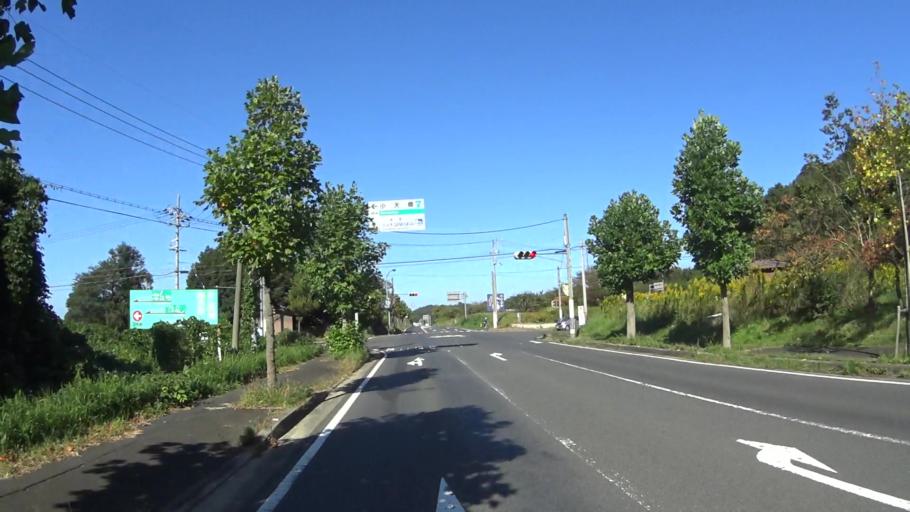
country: JP
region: Hyogo
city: Toyooka
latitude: 35.6266
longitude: 134.9290
